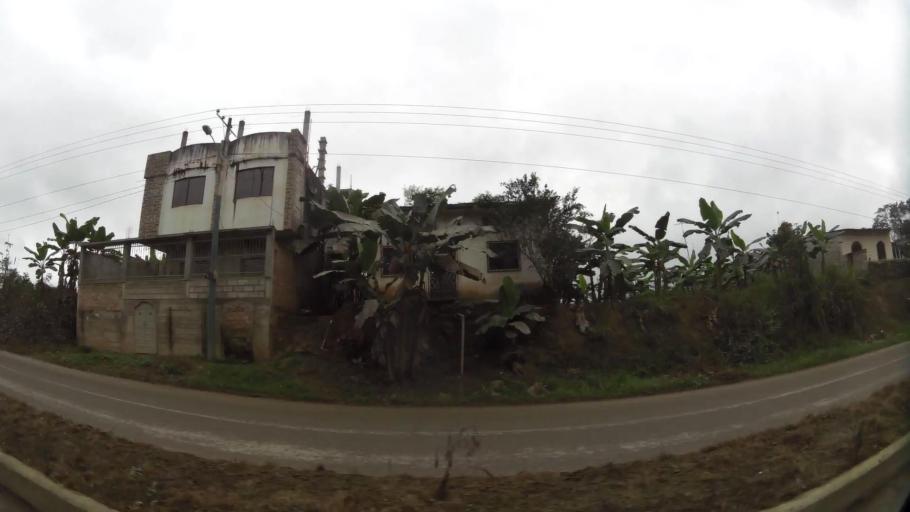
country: EC
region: El Oro
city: Pasaje
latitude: -3.3286
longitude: -79.7765
